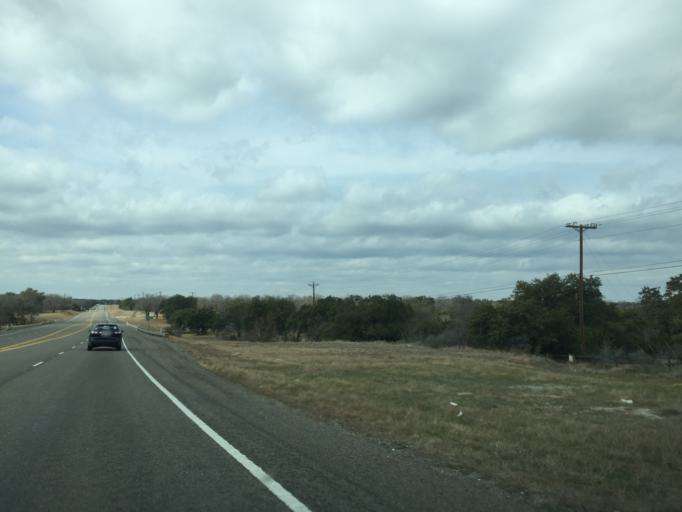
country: US
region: Texas
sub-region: Burnet County
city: Meadowlakes
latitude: 30.4929
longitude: -98.2382
